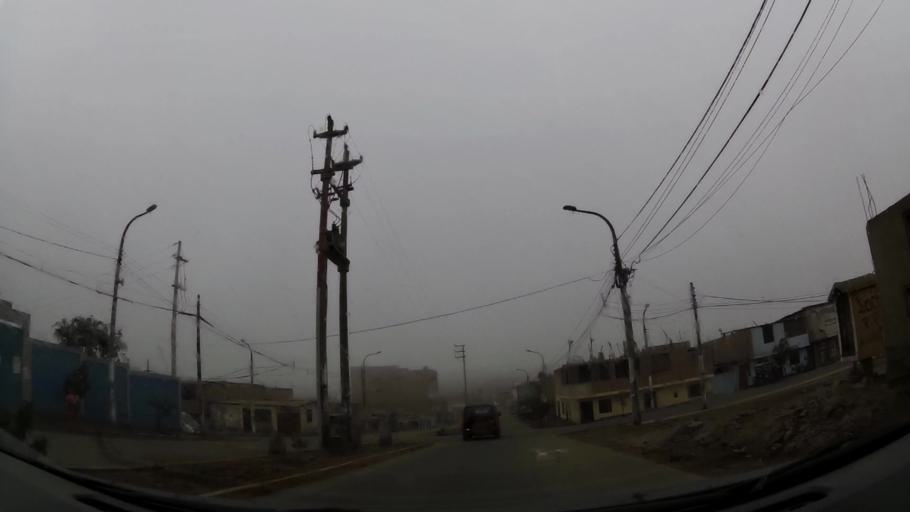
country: PE
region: Lima
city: Ventanilla
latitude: -11.8305
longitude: -77.1052
